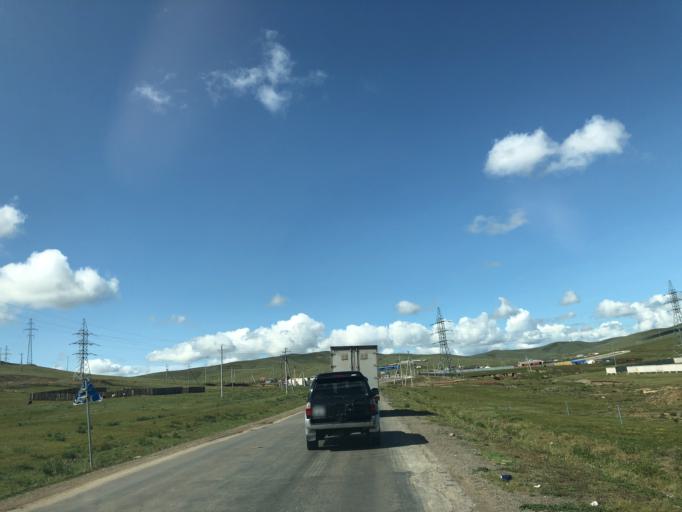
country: MN
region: Ulaanbaatar
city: Ulaanbaatar
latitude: 47.9232
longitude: 106.6237
